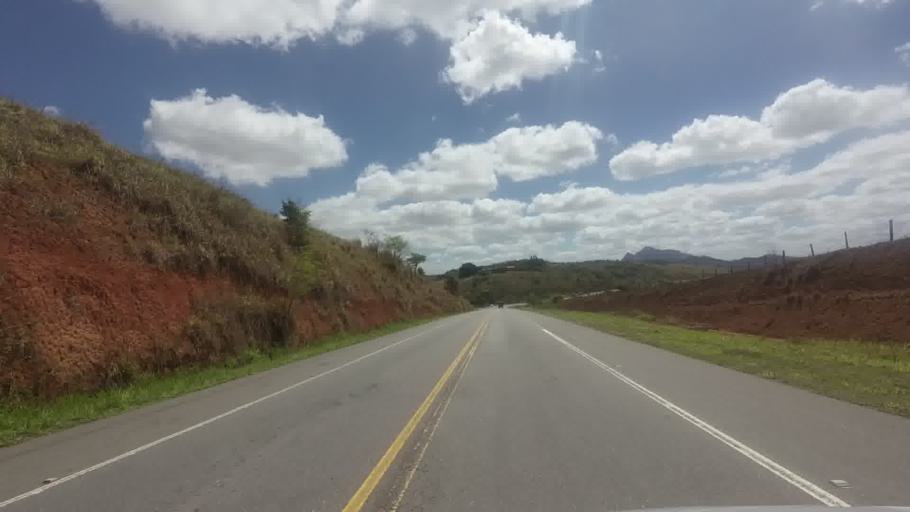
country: BR
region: Minas Gerais
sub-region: Recreio
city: Recreio
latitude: -21.6765
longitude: -42.3928
